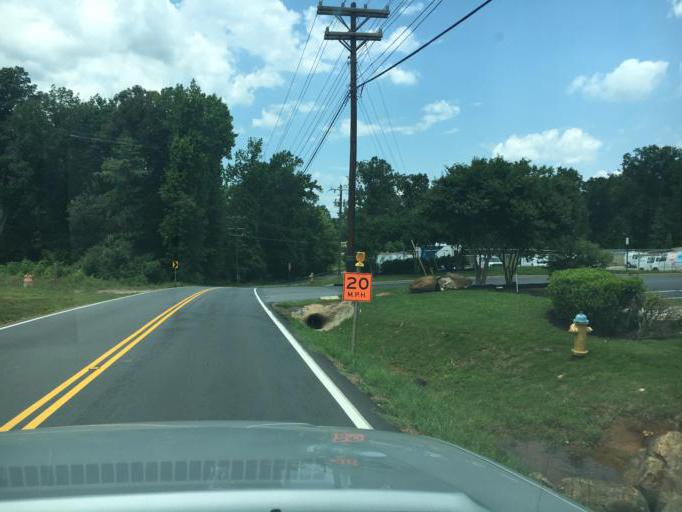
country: US
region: South Carolina
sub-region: Greenville County
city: Five Forks
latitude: 34.8578
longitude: -82.2341
